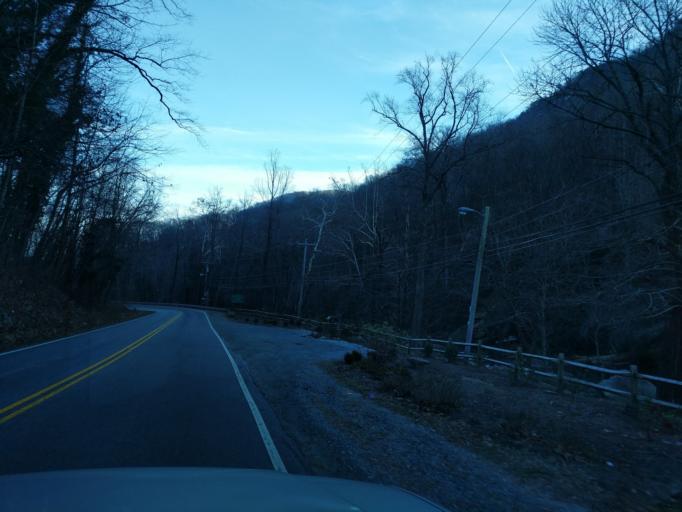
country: US
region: North Carolina
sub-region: Rutherford County
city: Lake Lure
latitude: 35.4460
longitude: -82.2749
